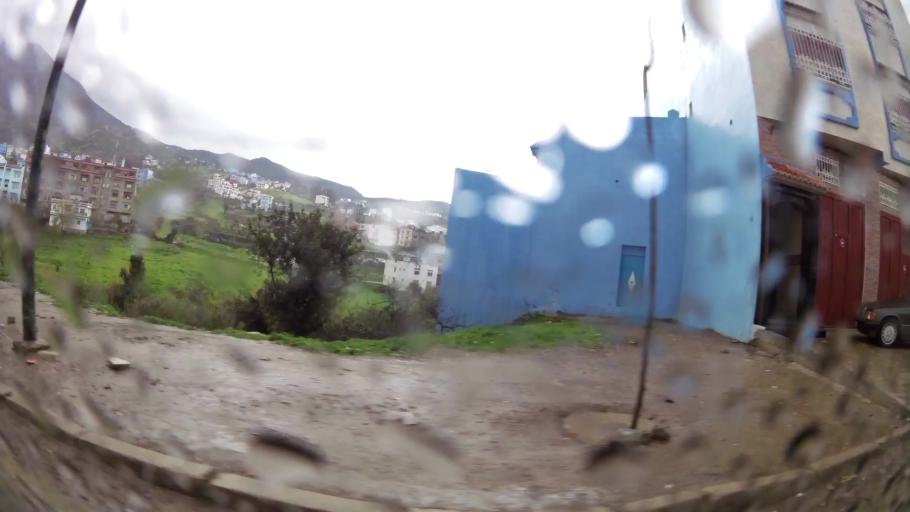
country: MA
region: Tanger-Tetouan
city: Chefchaouene
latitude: 35.1647
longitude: -5.2645
